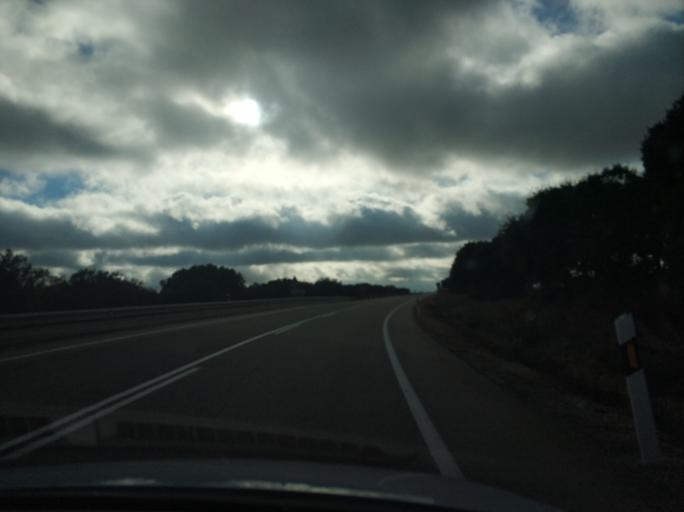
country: ES
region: Castille and Leon
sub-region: Provincia de Soria
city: Fuentecambron
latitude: 41.5000
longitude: -3.3064
